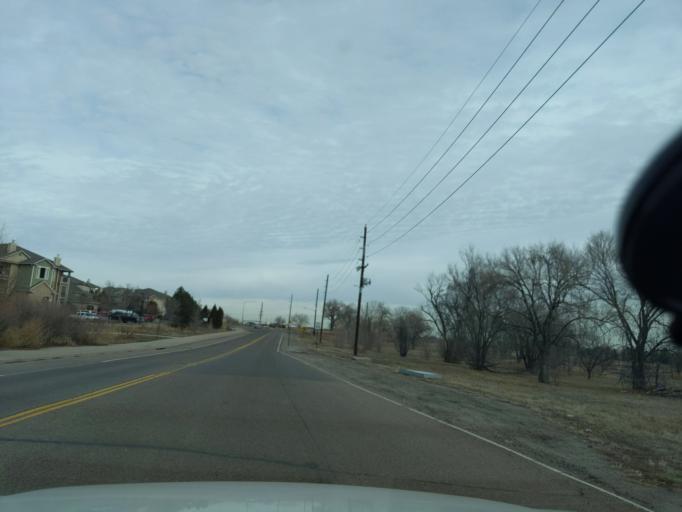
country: US
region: Colorado
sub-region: Adams County
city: Thornton
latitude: 39.8670
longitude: -104.9451
